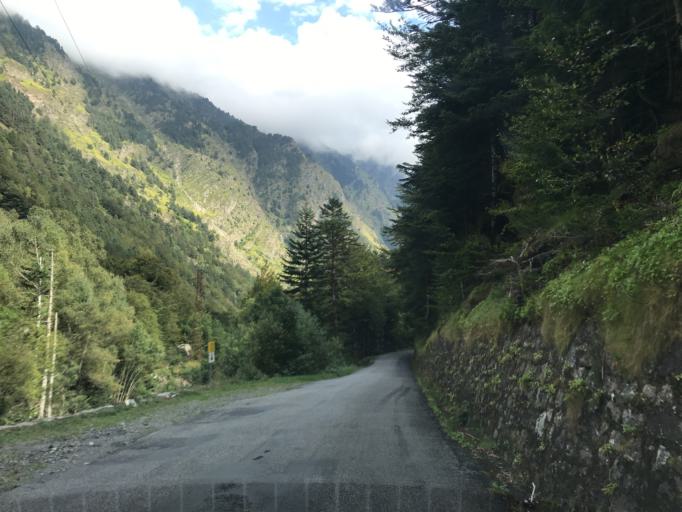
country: FR
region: Midi-Pyrenees
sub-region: Departement des Hautes-Pyrenees
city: Saint-Lary-Soulan
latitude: 42.8152
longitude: 0.2078
